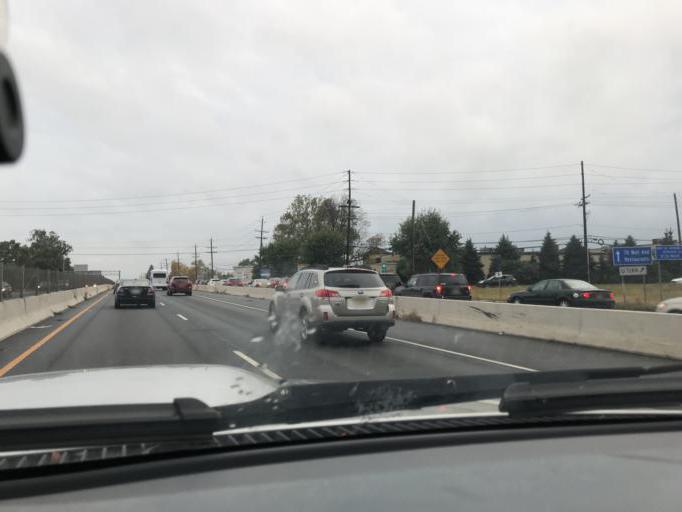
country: US
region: New Jersey
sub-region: Mercer County
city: Lawrenceville
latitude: 40.2975
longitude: -74.6792
